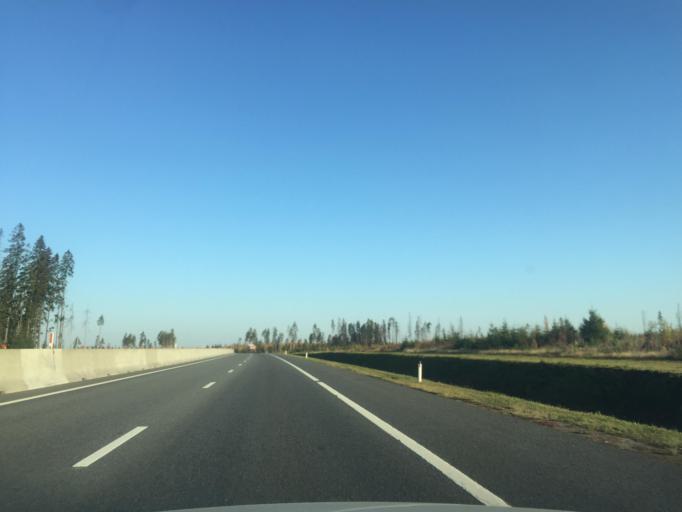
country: RU
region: Leningrad
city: Sosnovo
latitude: 60.5366
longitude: 30.1626
